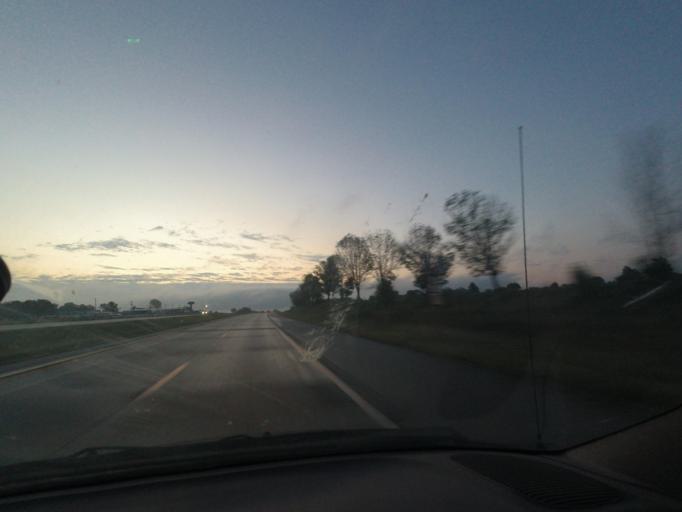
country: US
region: Missouri
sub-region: Linn County
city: Brookfield
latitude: 39.7710
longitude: -93.0644
